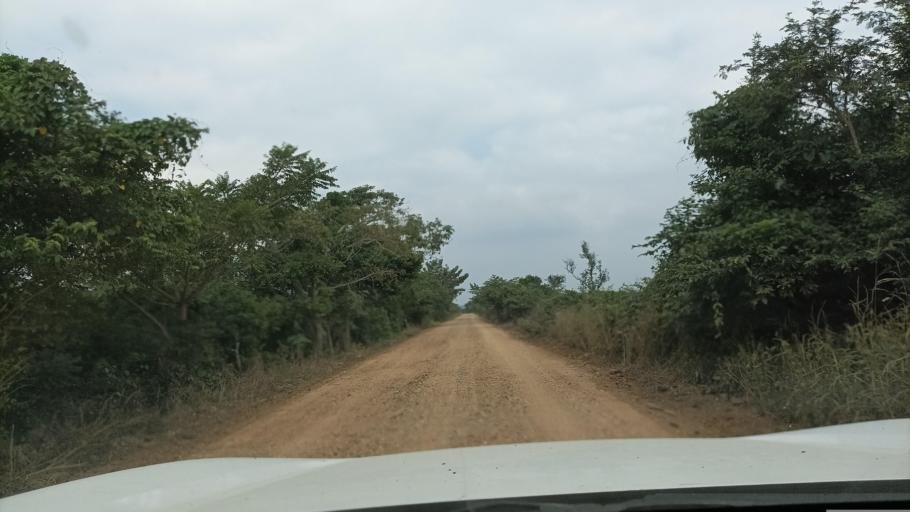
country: MX
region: Veracruz
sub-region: Texistepec
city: San Lorenzo Tenochtitlan
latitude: 17.7753
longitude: -94.7980
